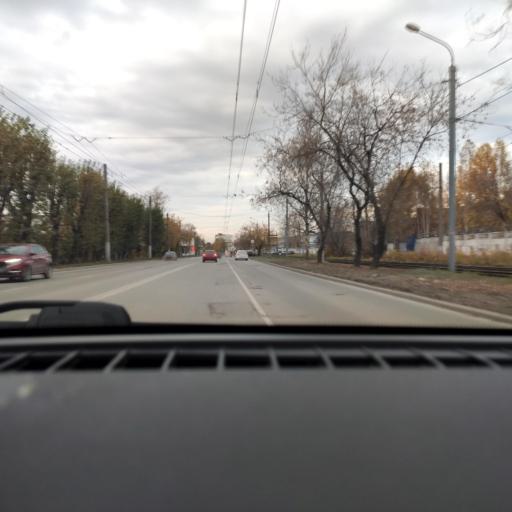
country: RU
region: Perm
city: Perm
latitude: 57.9699
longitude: 56.2456
